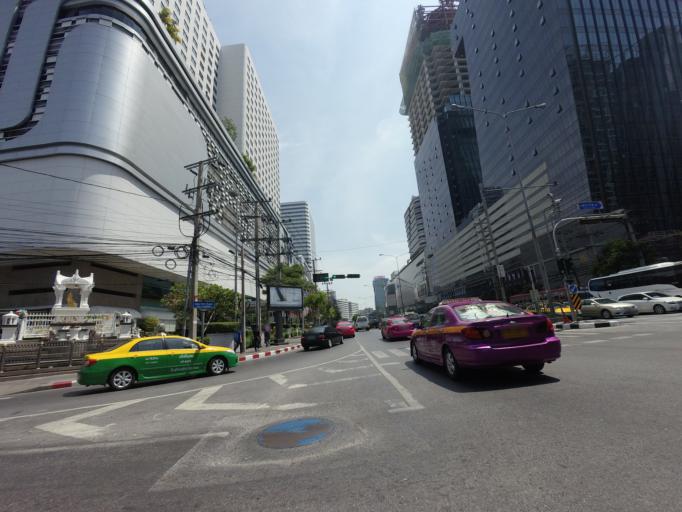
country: TH
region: Bangkok
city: Din Daeng
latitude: 13.7562
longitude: 100.5649
